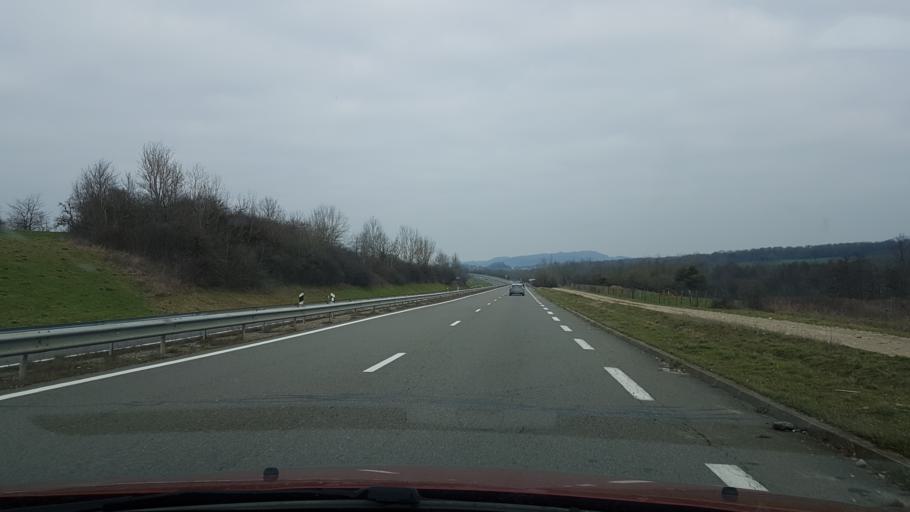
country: FR
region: Franche-Comte
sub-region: Departement du Jura
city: Lons-le-Saunier
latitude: 46.7262
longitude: 5.5579
